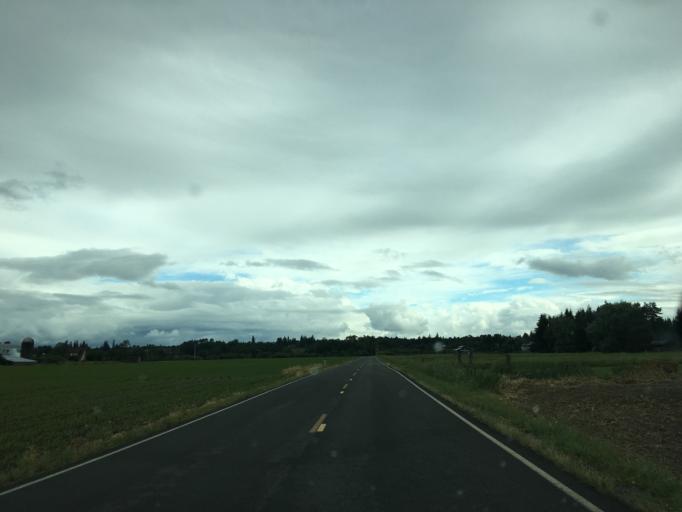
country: US
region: Washington
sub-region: Whatcom County
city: Nooksack
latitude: 48.9750
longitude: -122.3090
